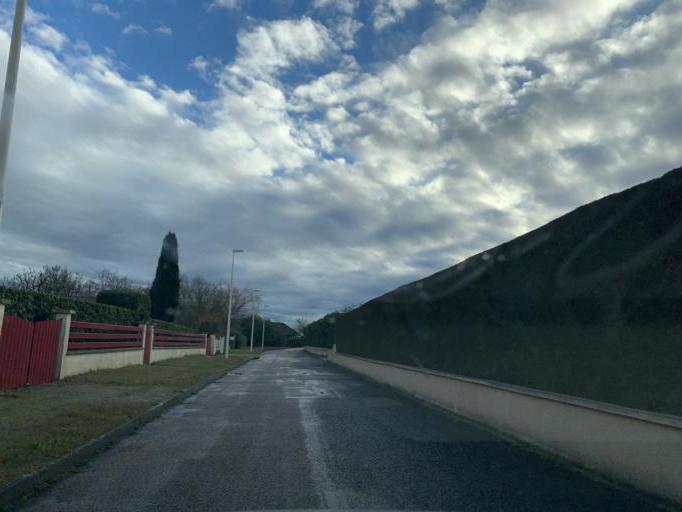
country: FR
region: Rhone-Alpes
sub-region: Departement du Rhone
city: Rillieux-la-Pape
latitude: 45.8129
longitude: 4.9246
